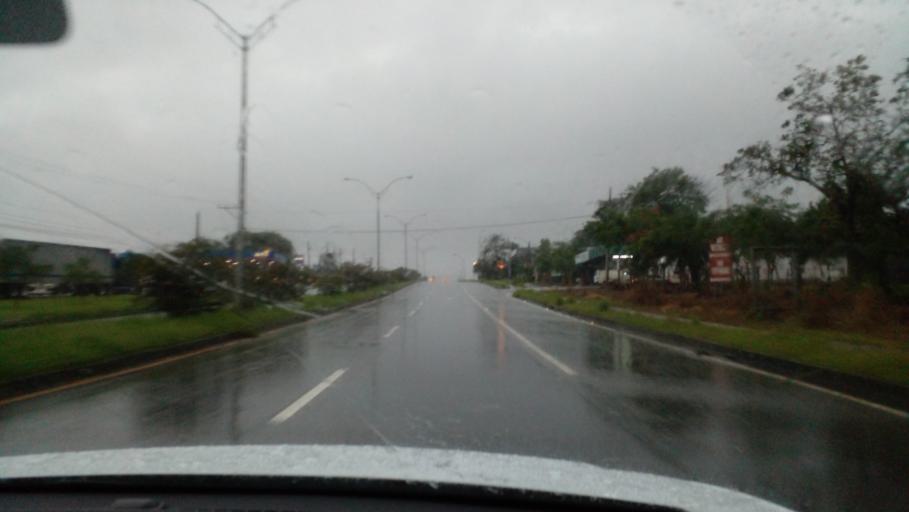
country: PA
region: Chiriqui
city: Las Lomas
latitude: 8.4279
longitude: -82.3895
